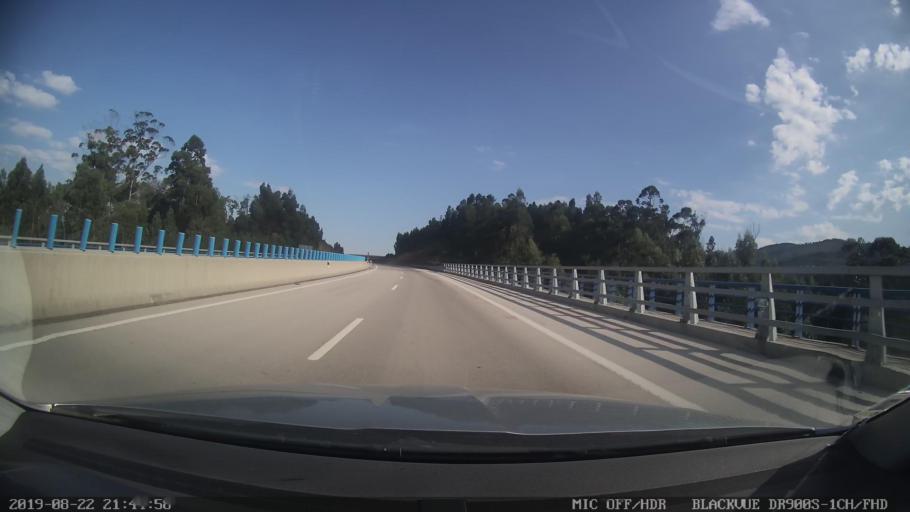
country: PT
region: Coimbra
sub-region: Penela
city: Penela
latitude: 39.9613
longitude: -8.3501
